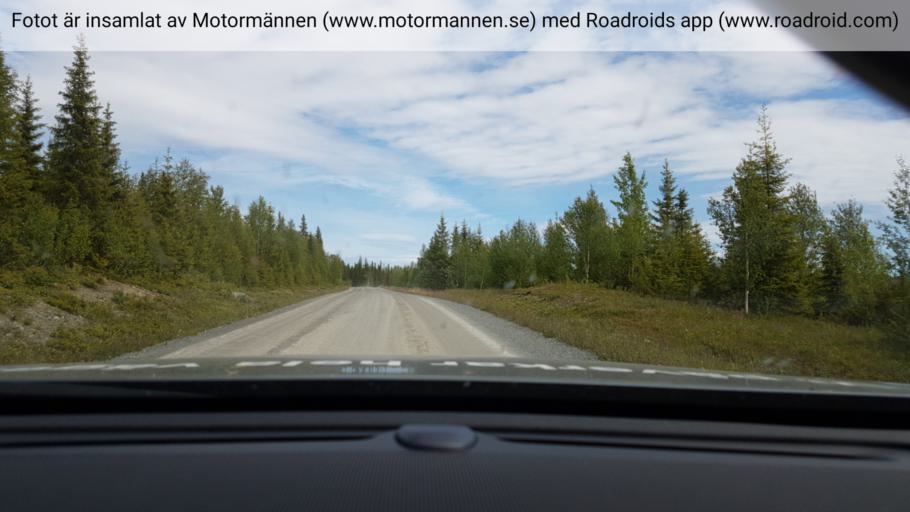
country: SE
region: Vaesterbotten
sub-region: Vilhelmina Kommun
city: Sjoberg
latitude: 65.1962
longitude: 16.1200
